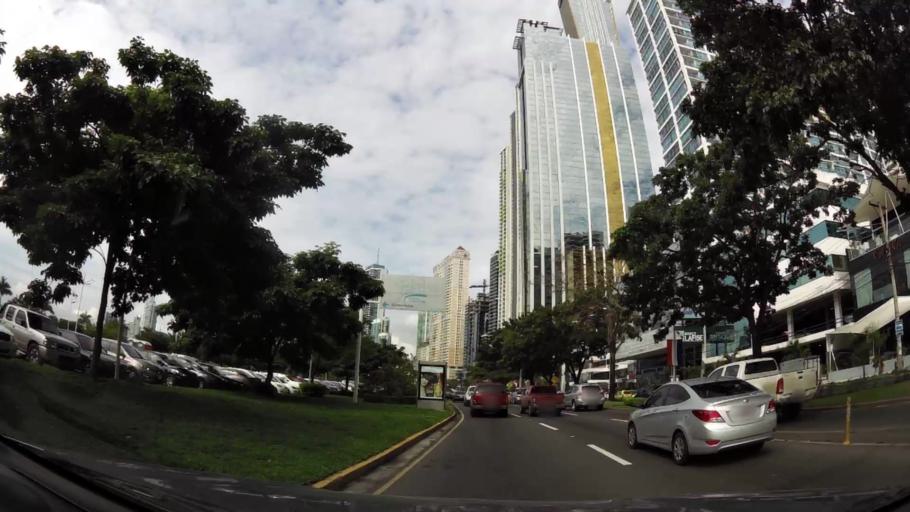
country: PA
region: Panama
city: Panama
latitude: 8.9755
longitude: -79.5206
